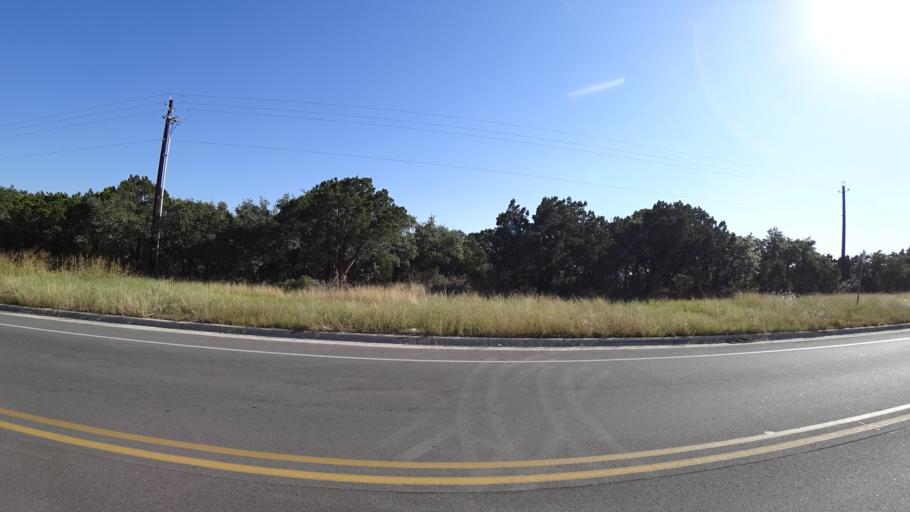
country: US
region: Texas
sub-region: Travis County
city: Hudson Bend
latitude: 30.3812
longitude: -97.8764
